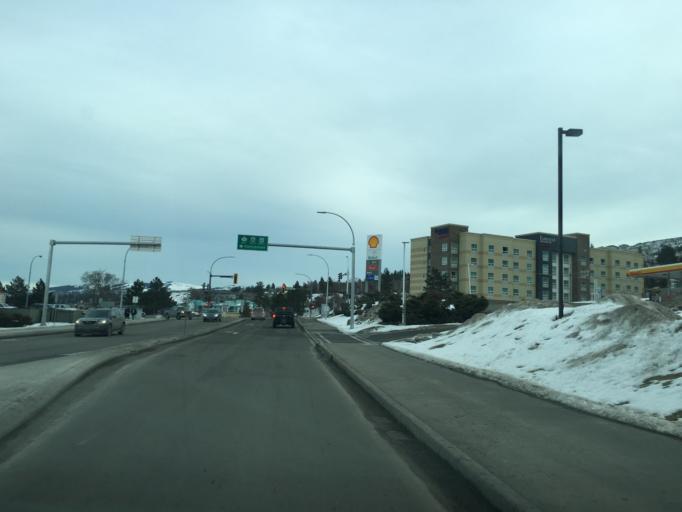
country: CA
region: British Columbia
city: Kamloops
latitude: 50.6522
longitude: -120.3814
